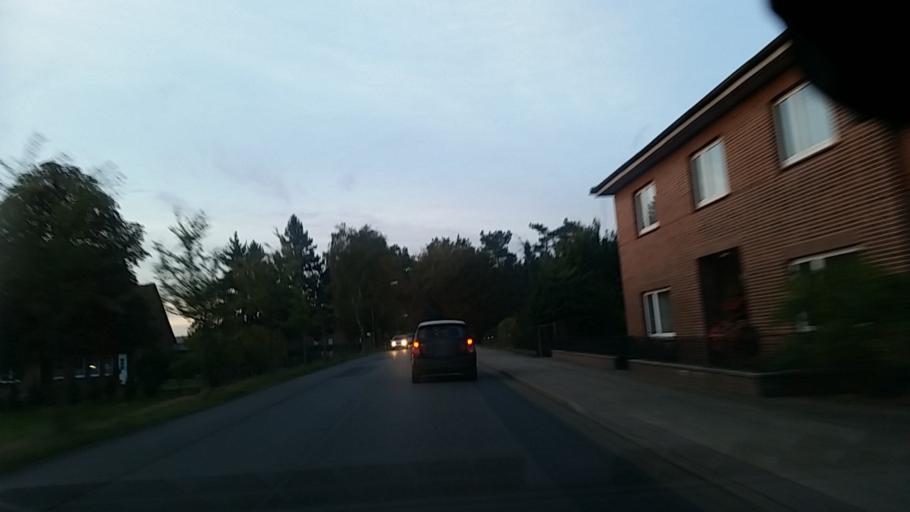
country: DE
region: Lower Saxony
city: Bodenteich
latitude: 52.8562
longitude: 10.6818
